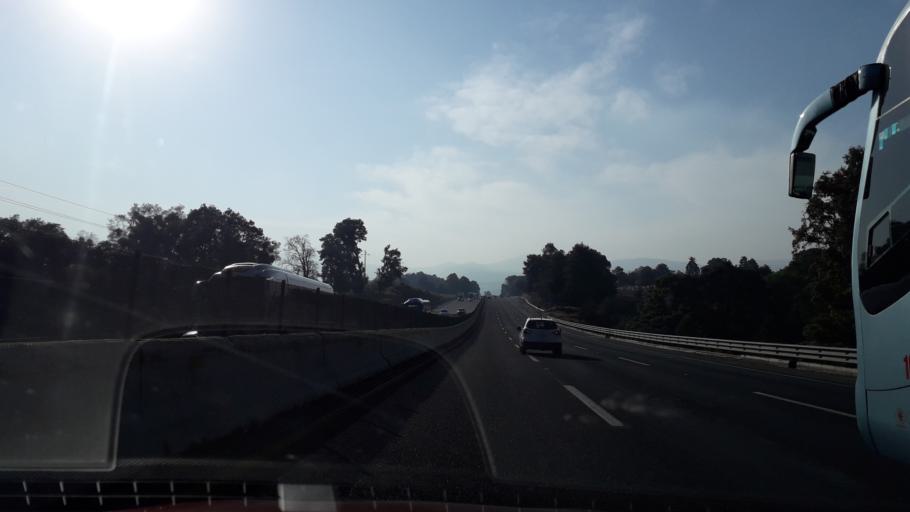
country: MX
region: Puebla
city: Santa Rita Tlahuapan
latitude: 19.3437
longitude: -98.5949
